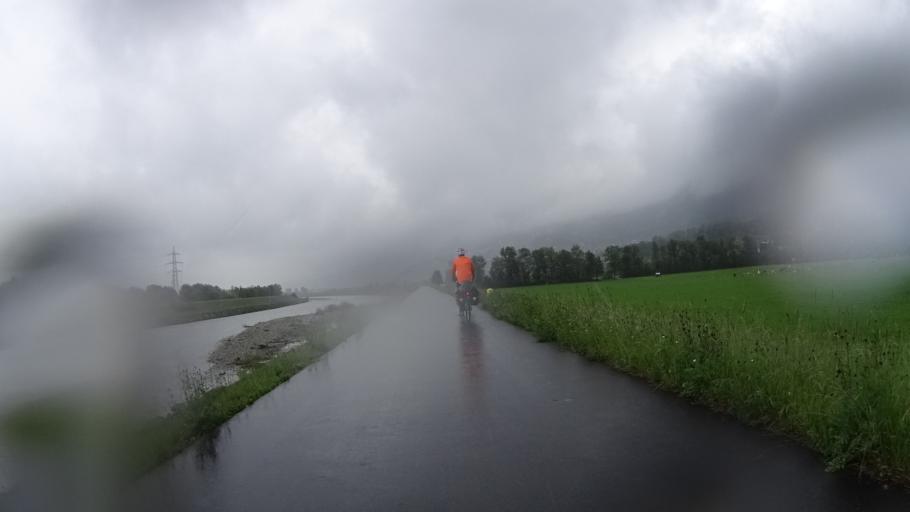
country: LI
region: Triesen
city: Triesen
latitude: 47.0910
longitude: 9.5181
